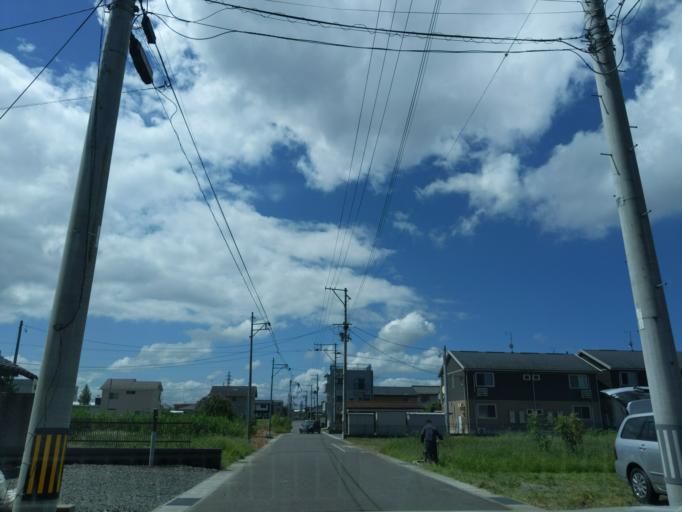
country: JP
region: Fukushima
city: Koriyama
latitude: 37.3861
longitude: 140.4060
